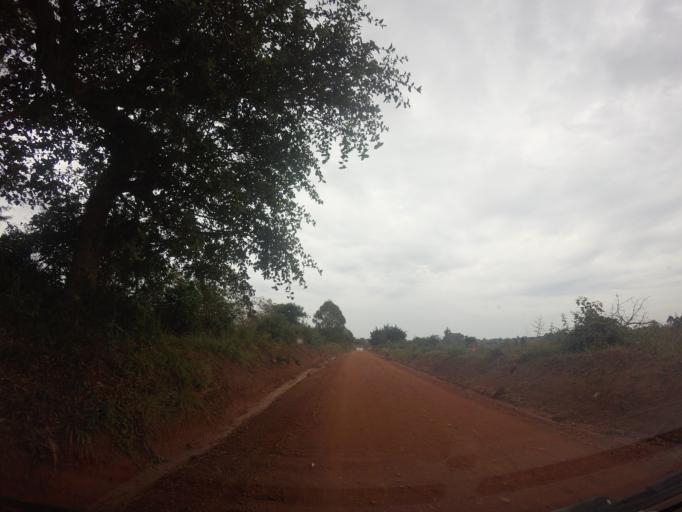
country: UG
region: Northern Region
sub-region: Arua District
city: Arua
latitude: 2.7914
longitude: 30.8687
